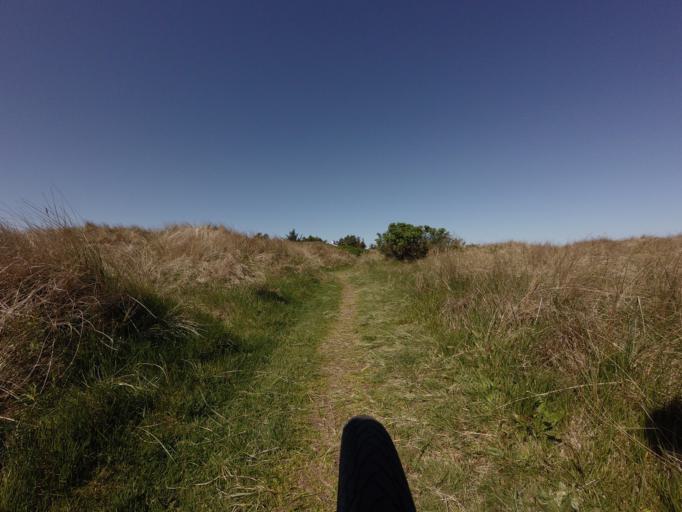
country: DK
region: North Denmark
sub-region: Jammerbugt Kommune
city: Pandrup
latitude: 57.3126
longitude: 9.6582
